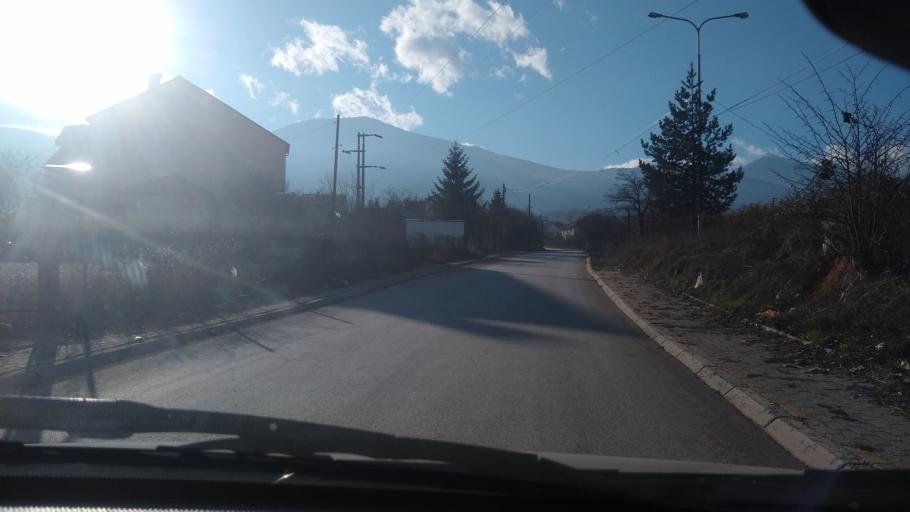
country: MK
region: Bitola
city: Bitola
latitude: 41.0210
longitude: 21.3189
